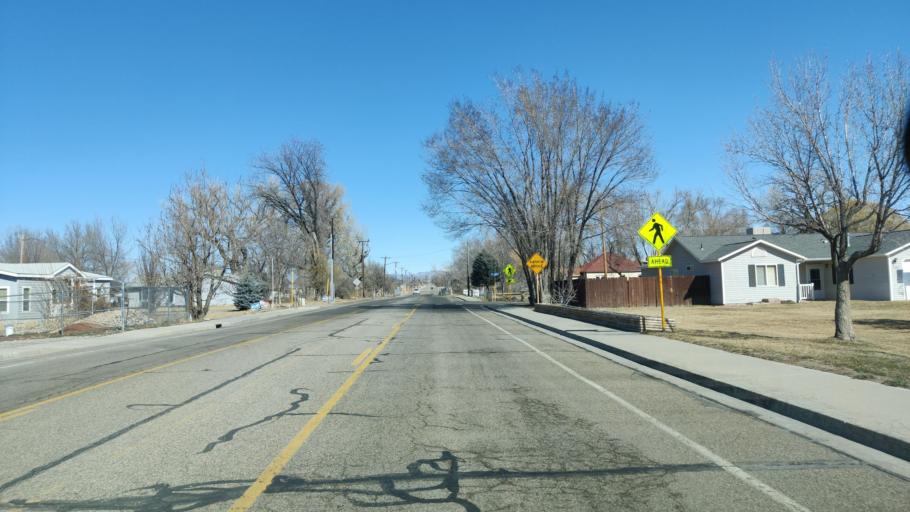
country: US
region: Colorado
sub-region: Mesa County
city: Fruita
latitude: 39.1691
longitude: -108.7197
